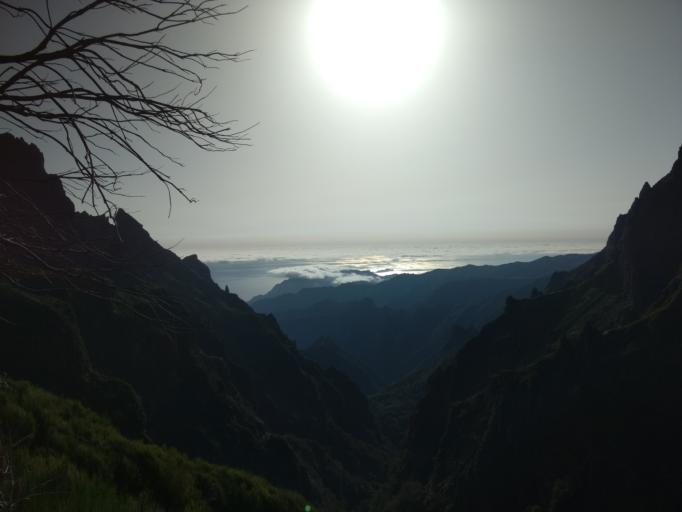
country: PT
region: Madeira
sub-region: Camara de Lobos
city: Curral das Freiras
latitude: 32.7437
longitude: -16.9378
